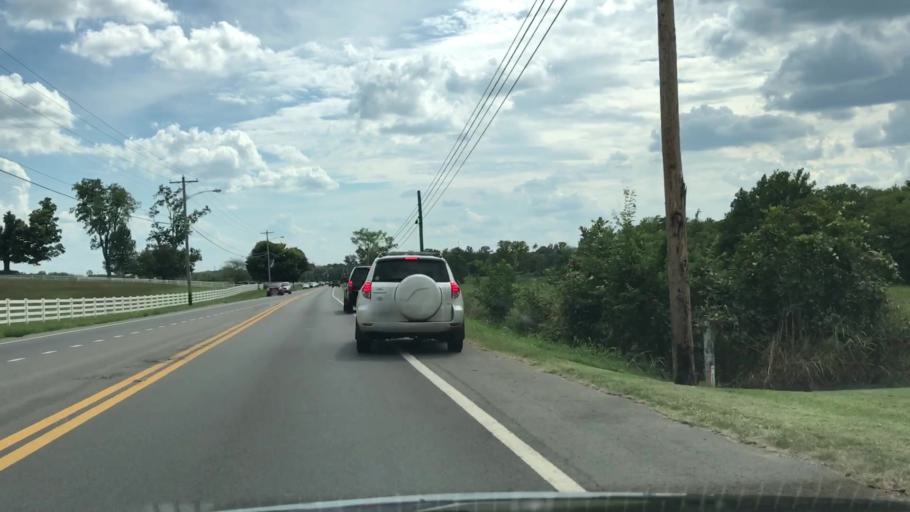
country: US
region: Tennessee
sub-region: Maury County
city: Spring Hill
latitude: 35.7647
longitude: -86.9199
